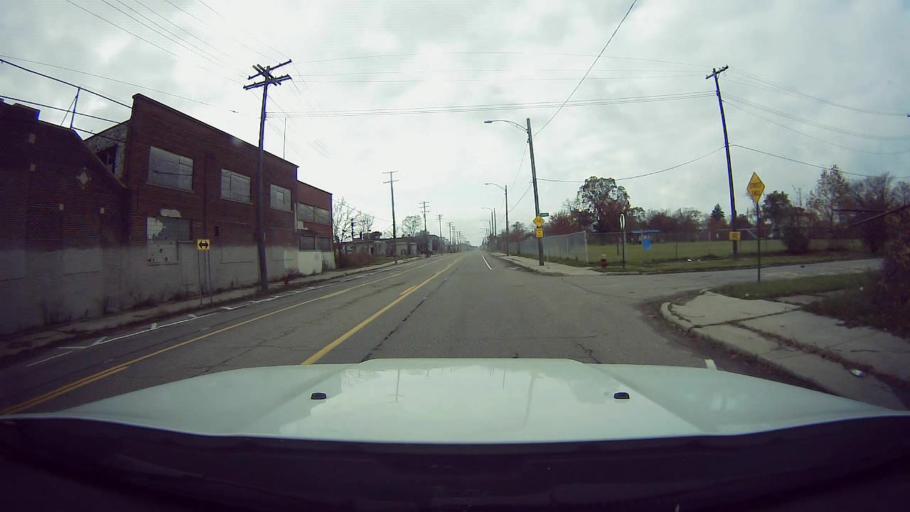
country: US
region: Michigan
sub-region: Wayne County
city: Highland Park
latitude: 42.4032
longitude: -83.1199
